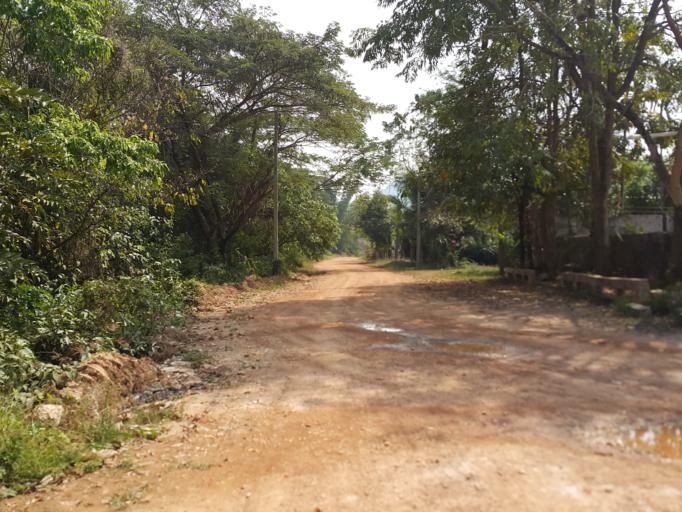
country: TH
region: Sukhothai
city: Thung Saliam
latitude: 17.3319
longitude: 99.4930
